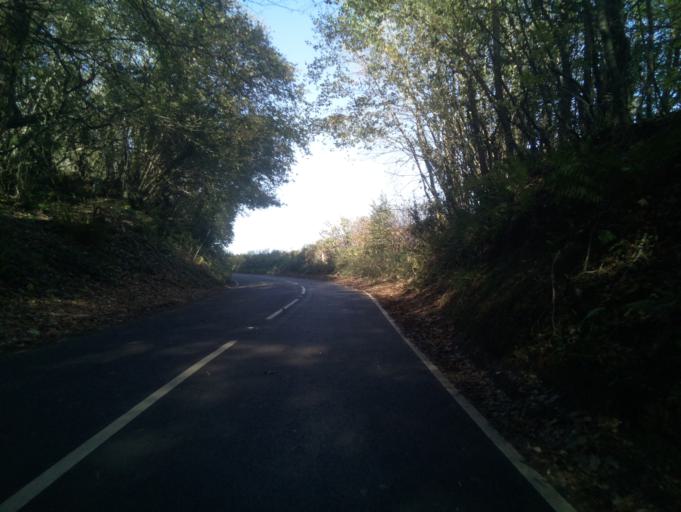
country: GB
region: England
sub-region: Dorset
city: Sherborne
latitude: 50.8409
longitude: -2.4888
